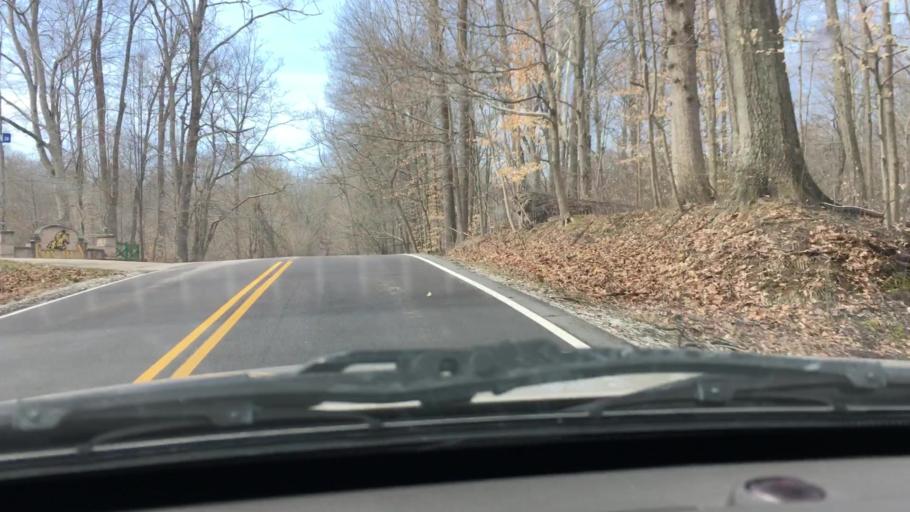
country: US
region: Indiana
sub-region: Morgan County
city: Martinsville
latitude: 39.4768
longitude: -86.4008
